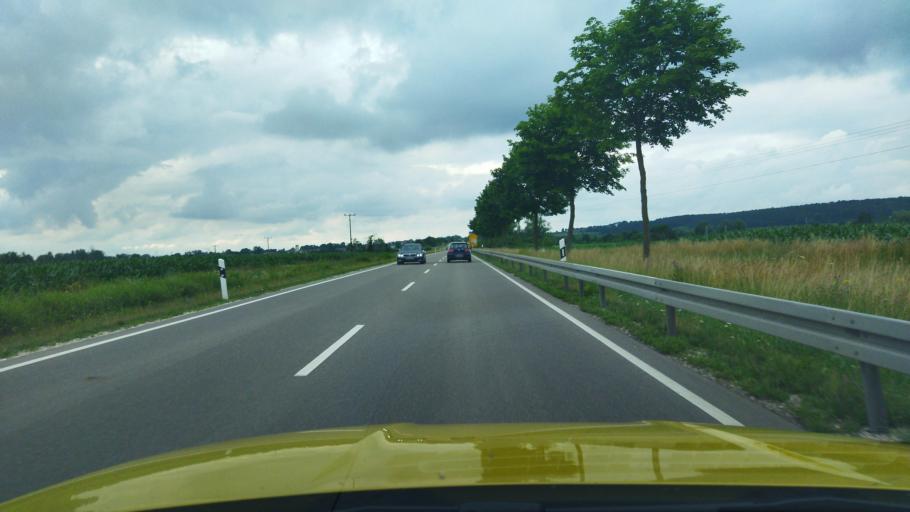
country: DE
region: Bavaria
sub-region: Regierungsbezirk Mittelfranken
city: Muhr am See
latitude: 49.1396
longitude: 10.7392
